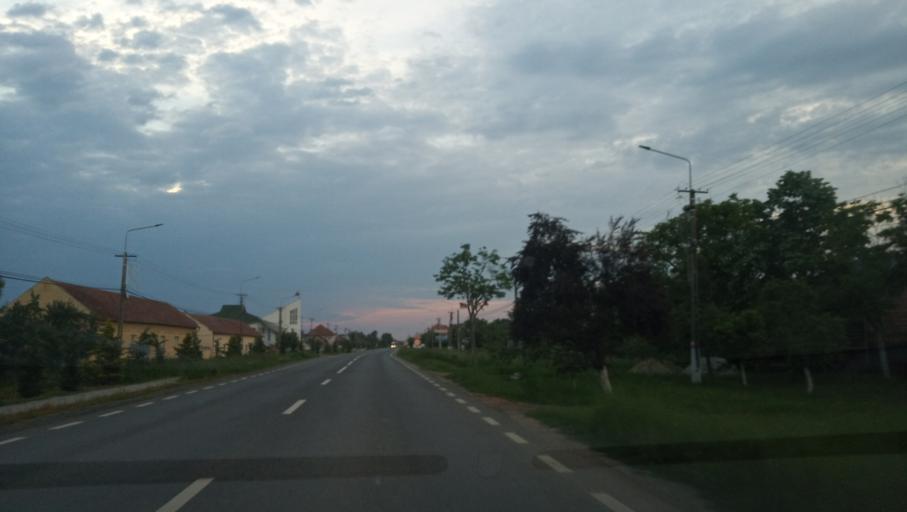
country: RO
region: Timis
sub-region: Comuna Jebel
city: Jebel
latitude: 45.5577
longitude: 21.2191
